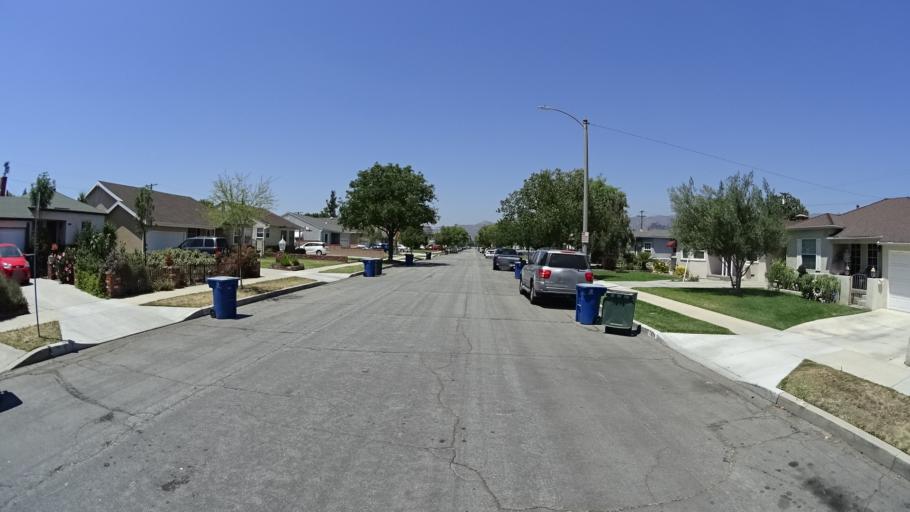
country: US
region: California
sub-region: Los Angeles County
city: Burbank
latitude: 34.1818
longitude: -118.3406
